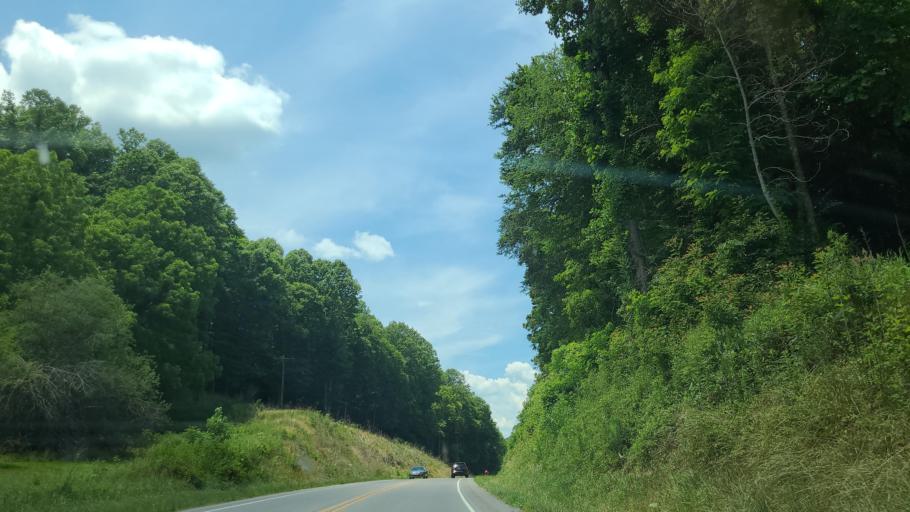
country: US
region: North Carolina
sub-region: Clay County
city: Hayesville
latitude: 35.0322
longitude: -83.8622
